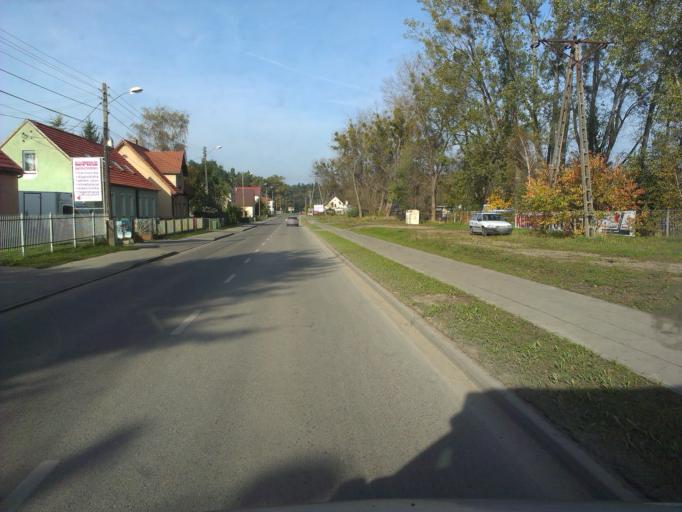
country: PL
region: West Pomeranian Voivodeship
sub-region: Powiat gryfinski
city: Stare Czarnowo
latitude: 53.3606
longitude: 14.7355
